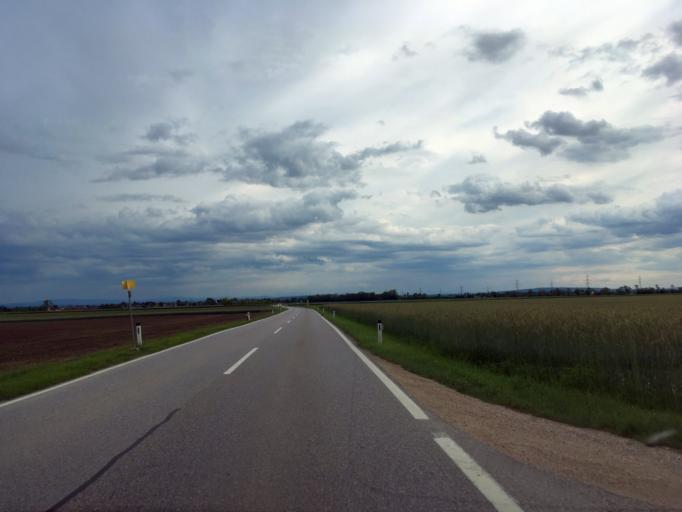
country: AT
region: Lower Austria
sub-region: Politischer Bezirk Tulln
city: Kirchberg am Wagram
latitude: 48.4211
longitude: 15.8948
